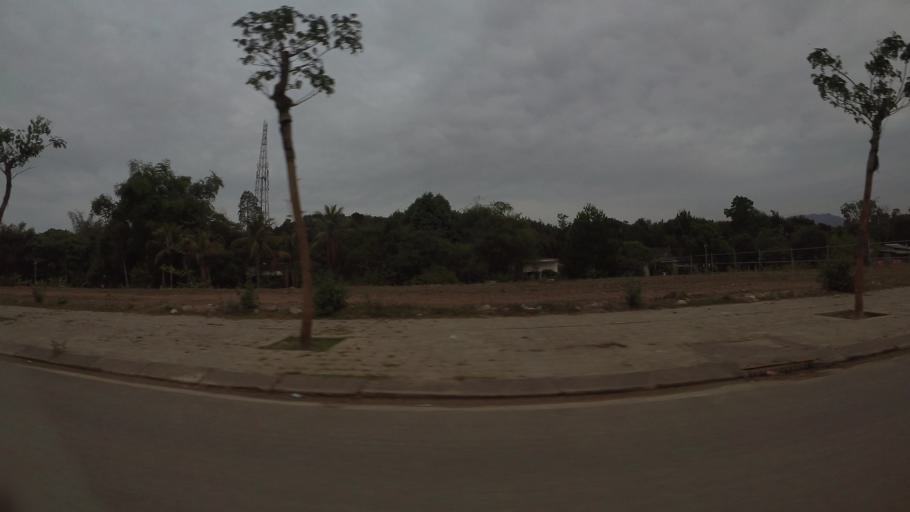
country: VN
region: Da Nang
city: Lien Chieu
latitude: 16.0953
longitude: 108.1119
